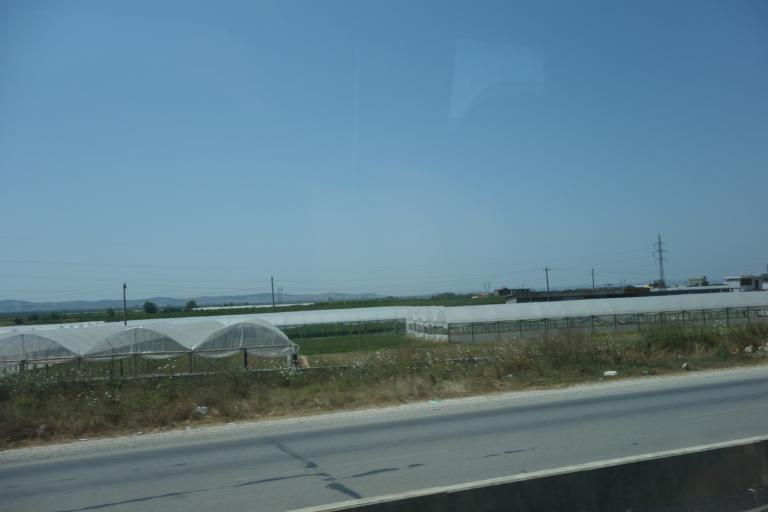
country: AL
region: Fier
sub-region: Rrethi i Lushnjes
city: Golem
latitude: 40.9900
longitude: 19.6689
